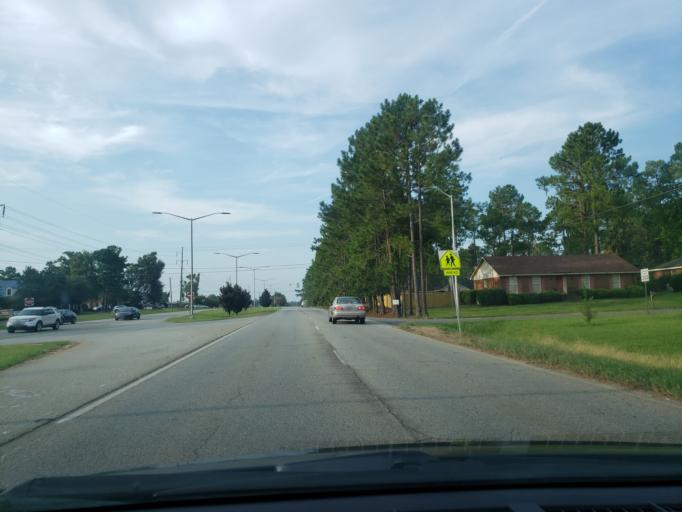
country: US
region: Georgia
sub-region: Dougherty County
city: Albany
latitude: 31.5930
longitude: -84.2196
